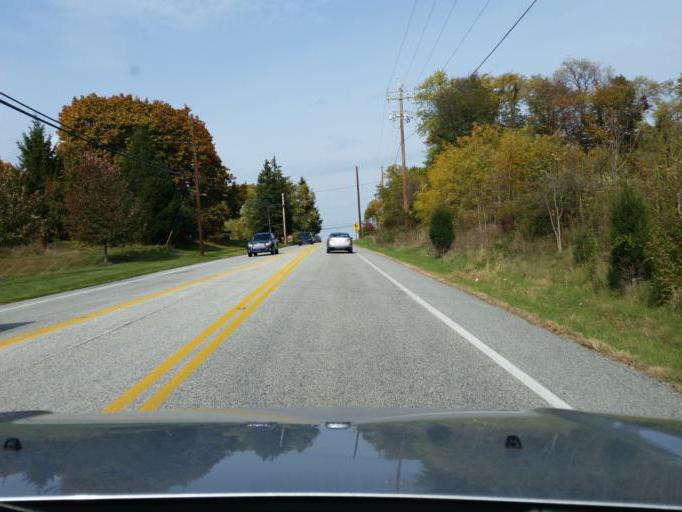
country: US
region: Pennsylvania
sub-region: Dauphin County
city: Skyline View
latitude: 40.3340
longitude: -76.7126
